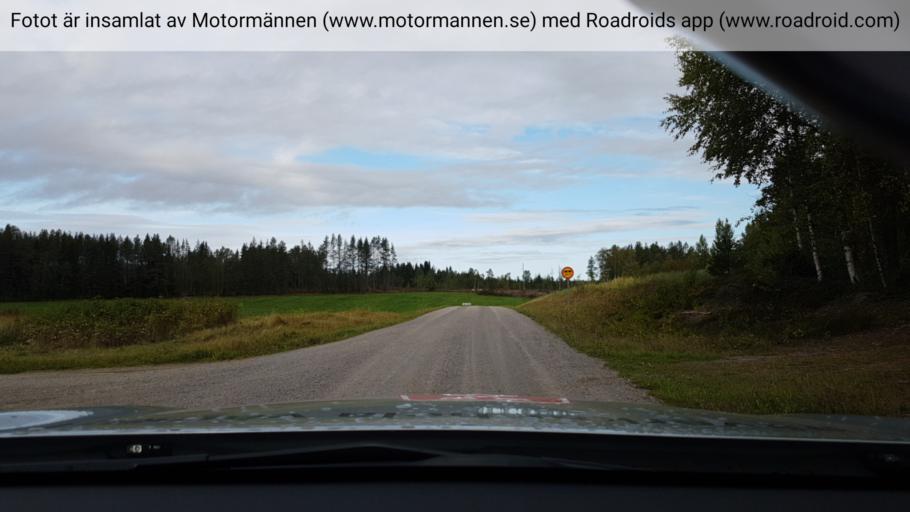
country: SE
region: Vaesterbotten
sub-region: Skelleftea Kommun
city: Byske
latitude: 65.1228
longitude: 21.2060
